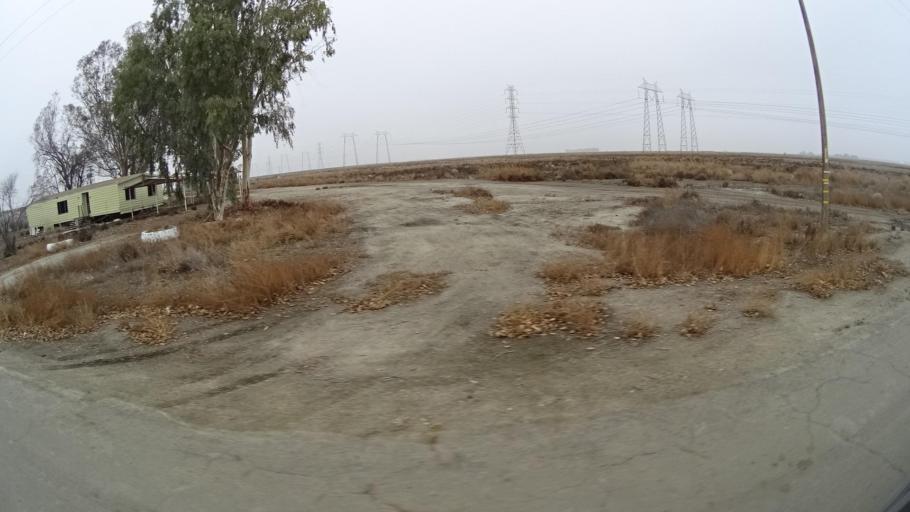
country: US
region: California
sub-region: Kern County
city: Lost Hills
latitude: 35.5866
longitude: -119.6002
